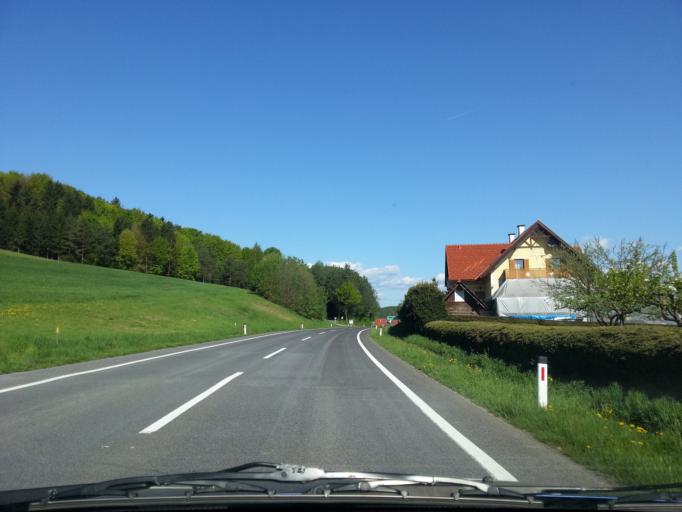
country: AT
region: Styria
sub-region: Politischer Bezirk Leibnitz
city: Arnfels
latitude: 46.6827
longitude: 15.3857
